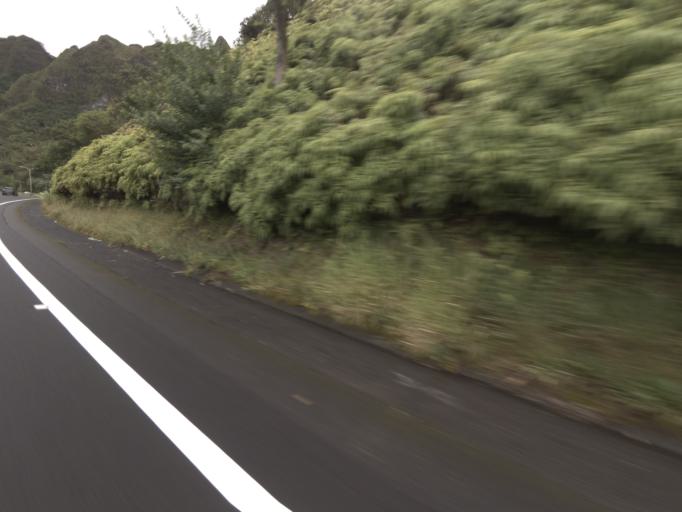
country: US
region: Hawaii
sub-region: Honolulu County
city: Kane'ohe
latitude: 21.3861
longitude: -157.8152
